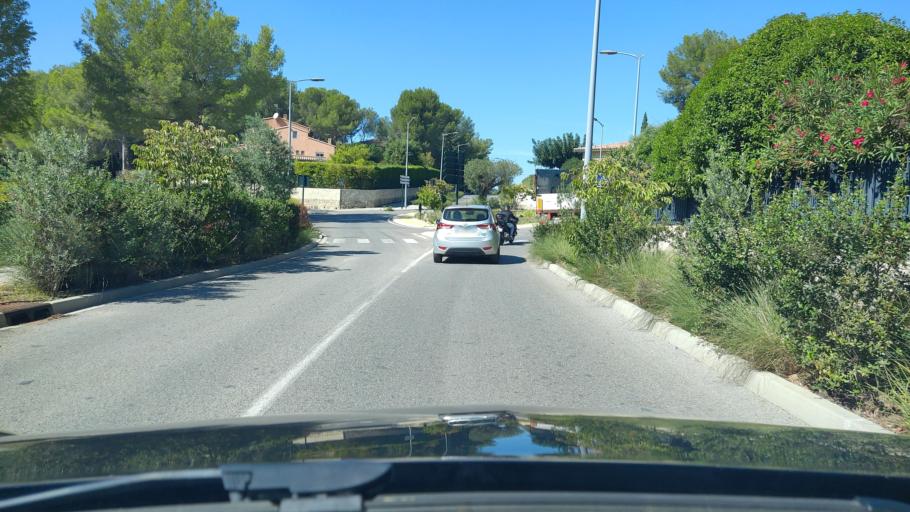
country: FR
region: Provence-Alpes-Cote d'Azur
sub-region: Departement du Var
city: Sanary-sur-Mer
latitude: 43.1399
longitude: 5.7820
